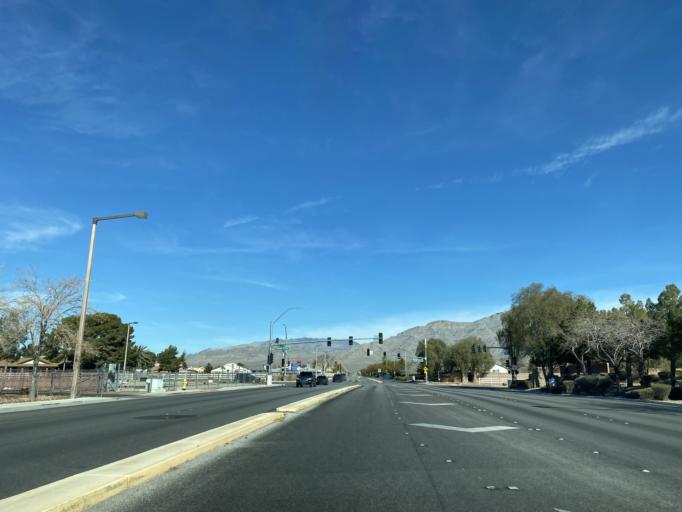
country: US
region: Nevada
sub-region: Clark County
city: North Las Vegas
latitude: 36.3040
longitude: -115.2240
